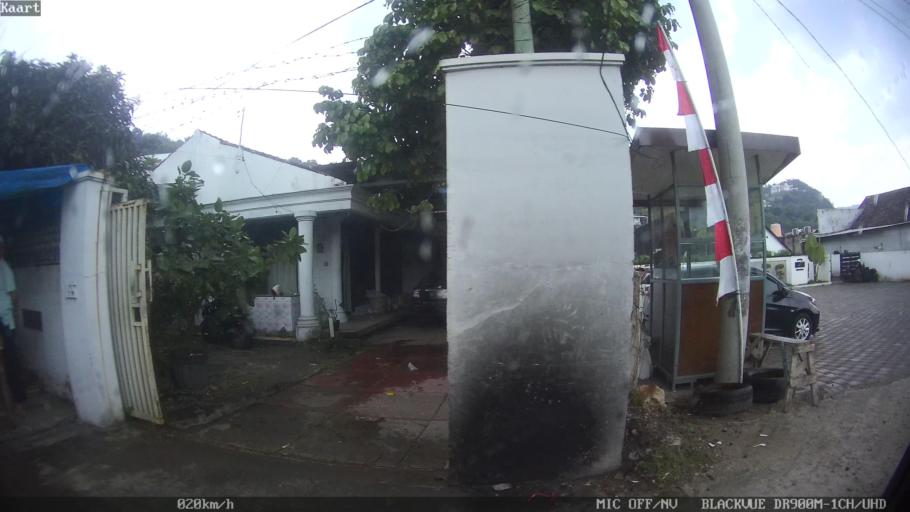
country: ID
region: Lampung
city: Bandarlampung
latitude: -5.4347
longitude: 105.2808
